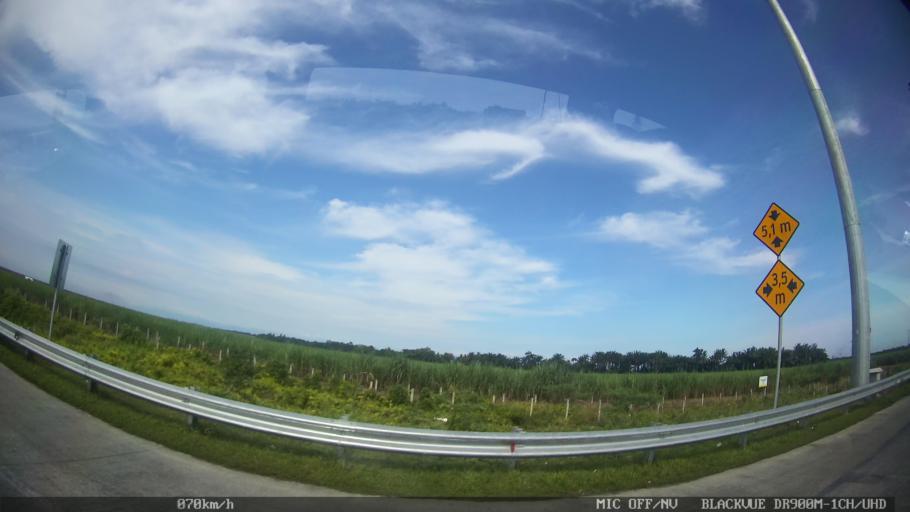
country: ID
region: North Sumatra
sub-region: Kabupaten Langkat
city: Stabat
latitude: 3.7183
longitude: 98.4937
